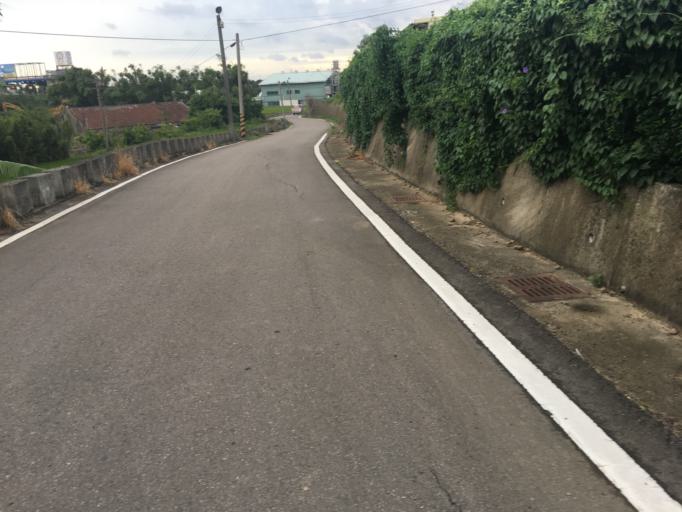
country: TW
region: Taiwan
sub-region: Hsinchu
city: Hsinchu
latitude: 24.7278
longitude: 120.9079
